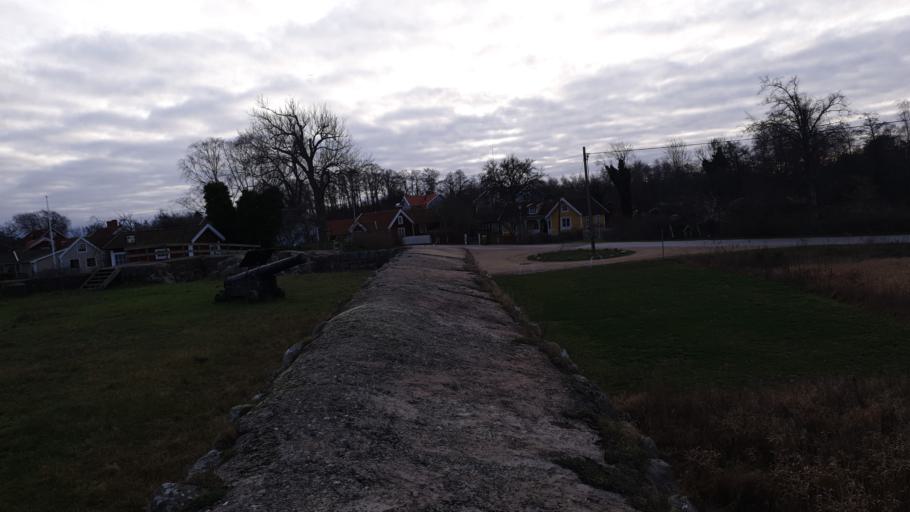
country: SE
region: Kalmar
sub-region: Torsas Kommun
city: Torsas
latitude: 56.2607
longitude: 16.0407
